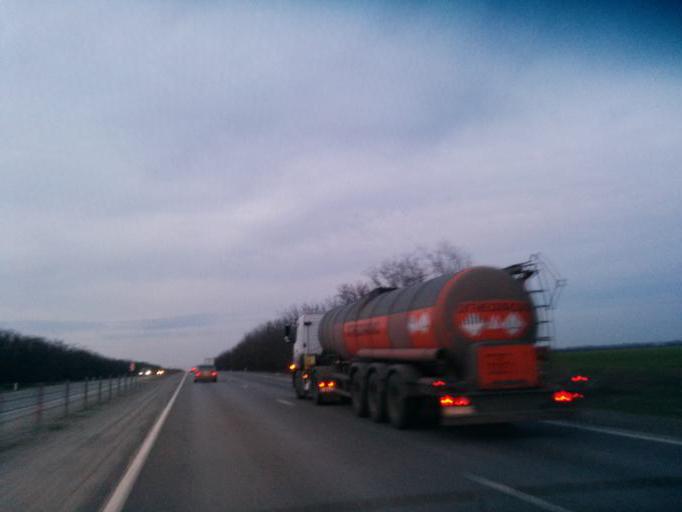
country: RU
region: Rostov
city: Grushevskaya
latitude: 47.5490
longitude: 39.9679
